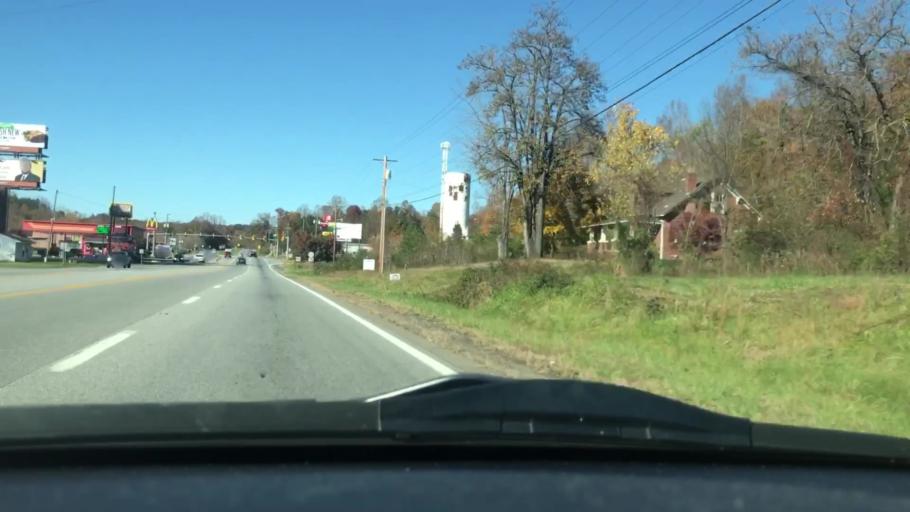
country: US
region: Virginia
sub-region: Henry County
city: Stanleytown
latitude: 36.7449
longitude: -79.9370
